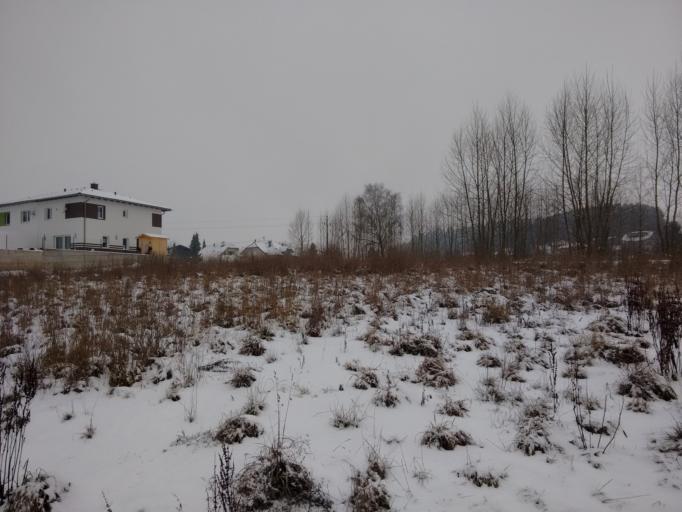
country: AT
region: Upper Austria
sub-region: Wels-Land
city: Buchkirchen
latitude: 48.1933
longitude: 13.9723
